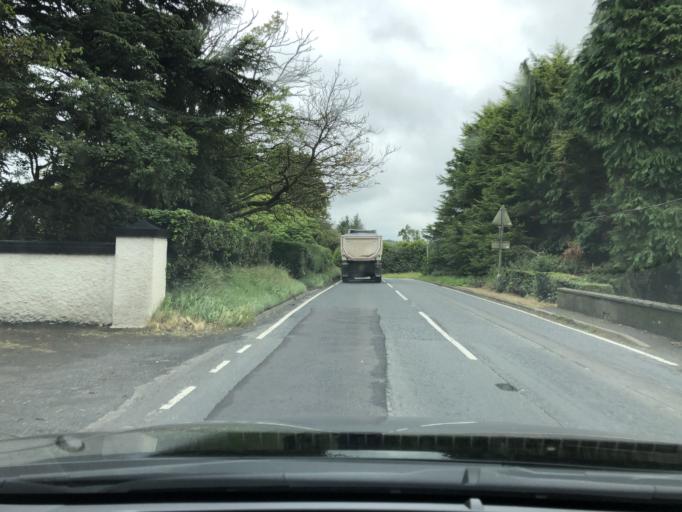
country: GB
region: Northern Ireland
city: Ballynahinch
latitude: 54.3634
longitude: -5.8600
